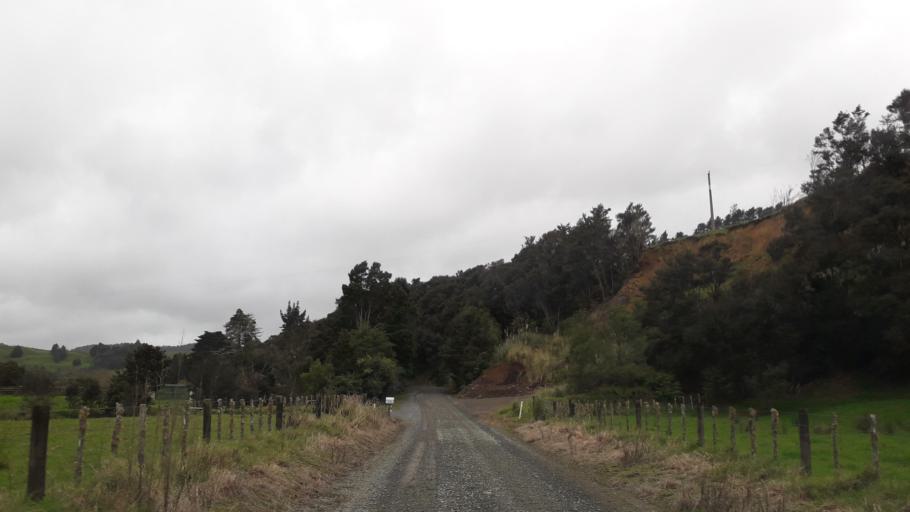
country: NZ
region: Northland
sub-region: Far North District
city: Waimate North
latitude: -35.1501
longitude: 173.7122
